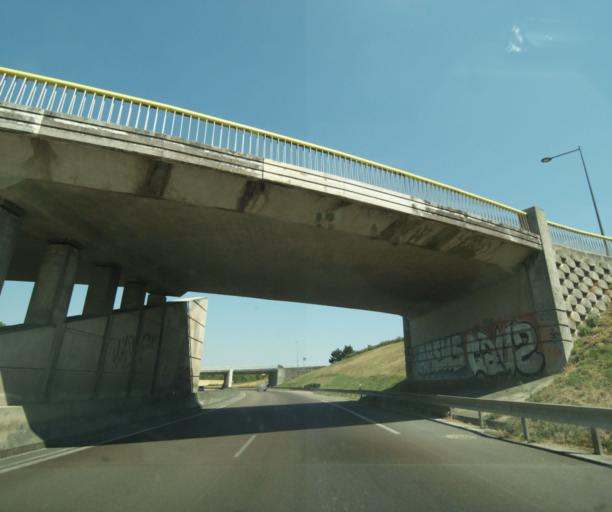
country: FR
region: Champagne-Ardenne
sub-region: Departement de la Marne
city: Saint-Memmie
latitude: 48.9621
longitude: 4.3907
